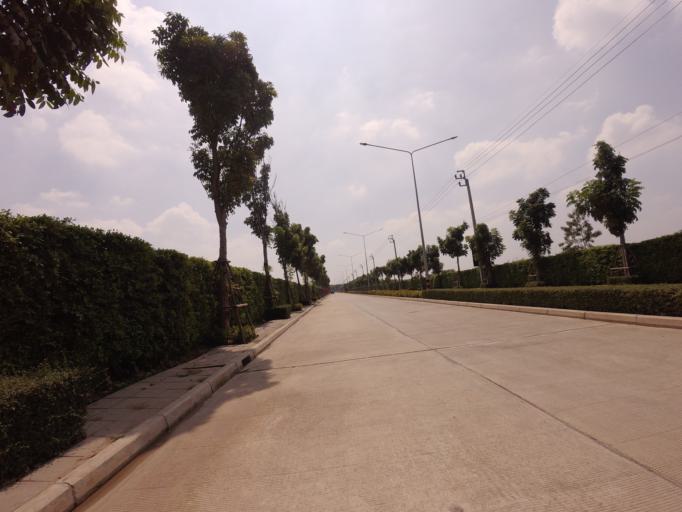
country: TH
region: Bangkok
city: Saphan Sung
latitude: 13.7527
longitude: 100.6706
